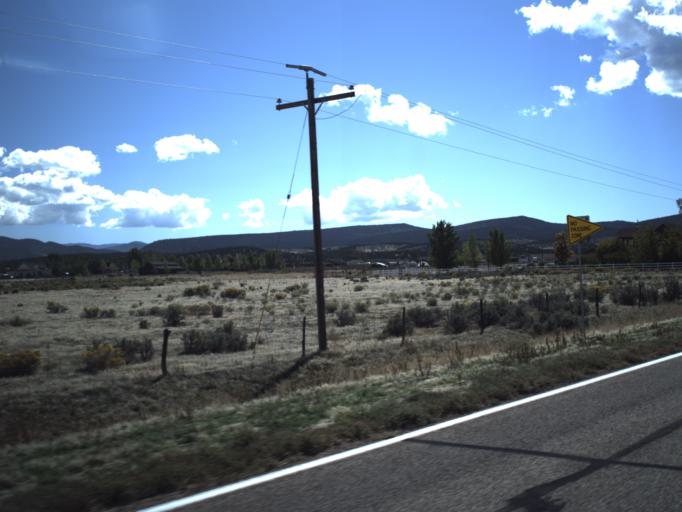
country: US
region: Utah
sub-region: Washington County
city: Enterprise
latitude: 37.6005
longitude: -113.6615
